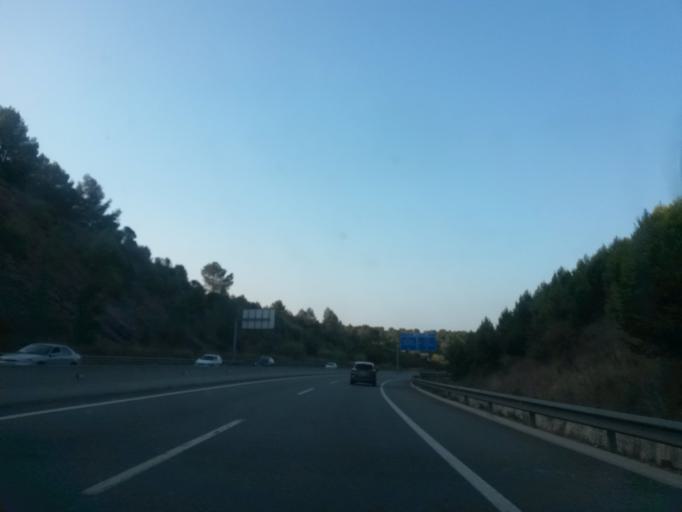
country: ES
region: Catalonia
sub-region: Provincia de Barcelona
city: Palleja
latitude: 41.4106
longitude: 1.9906
